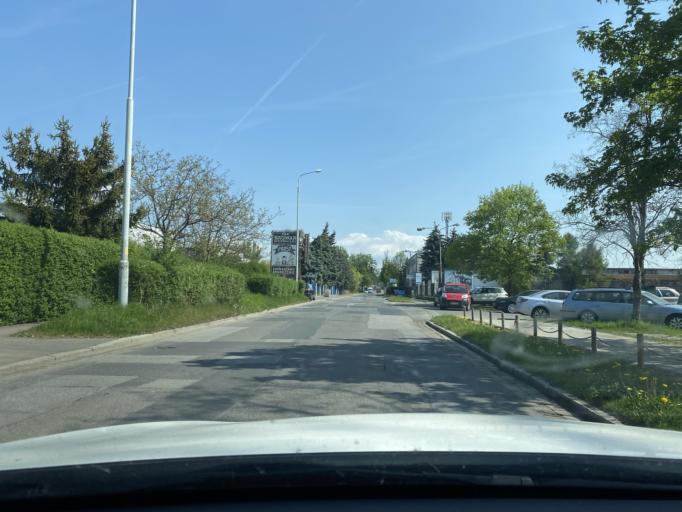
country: PL
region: Lower Silesian Voivodeship
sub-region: Powiat trzebnicki
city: Psary
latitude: 51.1499
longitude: 17.0223
